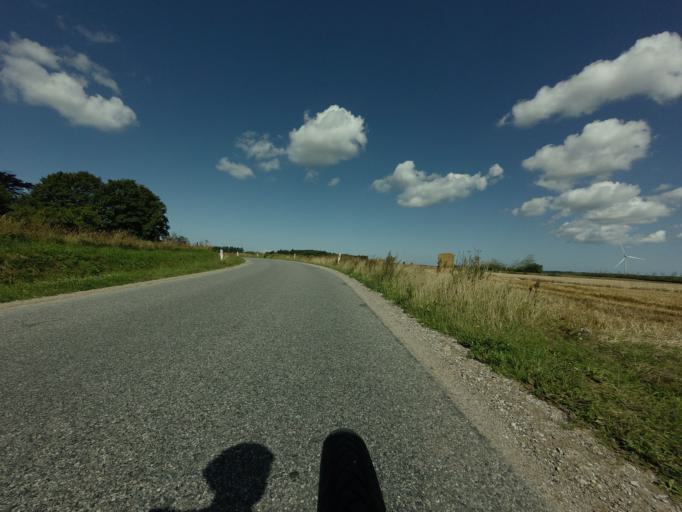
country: DK
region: North Denmark
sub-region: Hjorring Kommune
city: Hjorring
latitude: 57.4846
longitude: 9.9008
